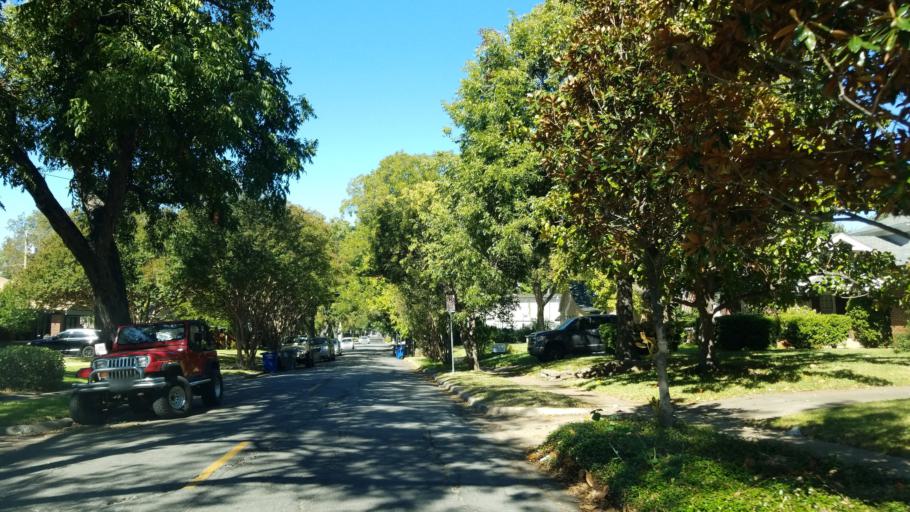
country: US
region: Texas
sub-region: Dallas County
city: Highland Park
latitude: 32.8080
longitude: -96.7576
